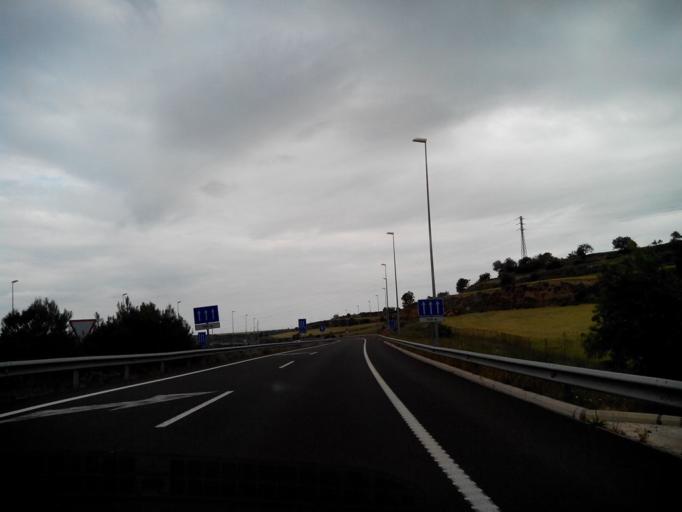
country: ES
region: Catalonia
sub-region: Provincia de Lleida
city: Cervera
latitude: 41.6845
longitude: 1.2800
